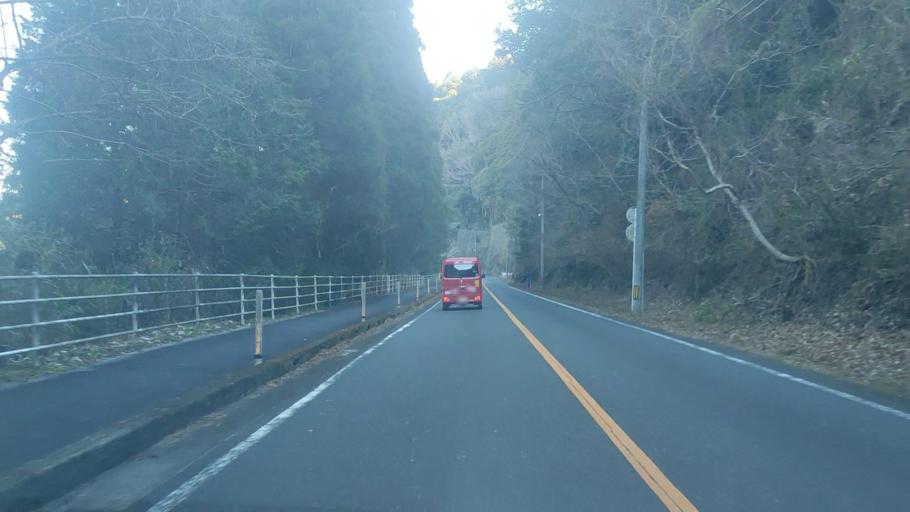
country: JP
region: Oita
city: Saiki
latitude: 32.7661
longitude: 131.8020
